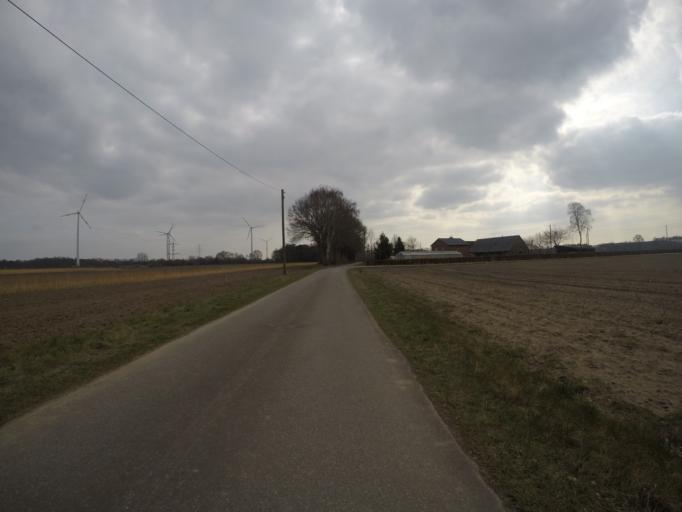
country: DE
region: North Rhine-Westphalia
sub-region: Regierungsbezirk Dusseldorf
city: Bocholt
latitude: 51.7945
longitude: 6.5711
